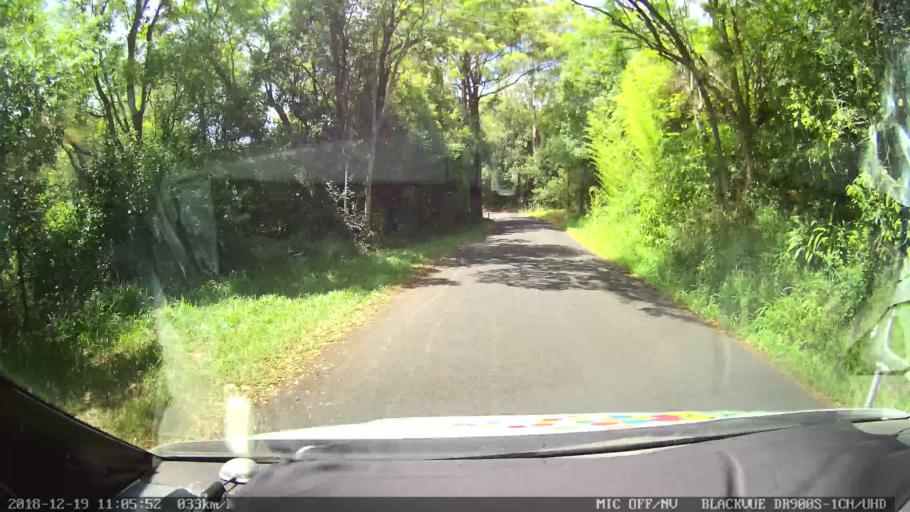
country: AU
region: New South Wales
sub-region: Lismore Municipality
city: Nimbin
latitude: -28.6197
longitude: 153.2652
